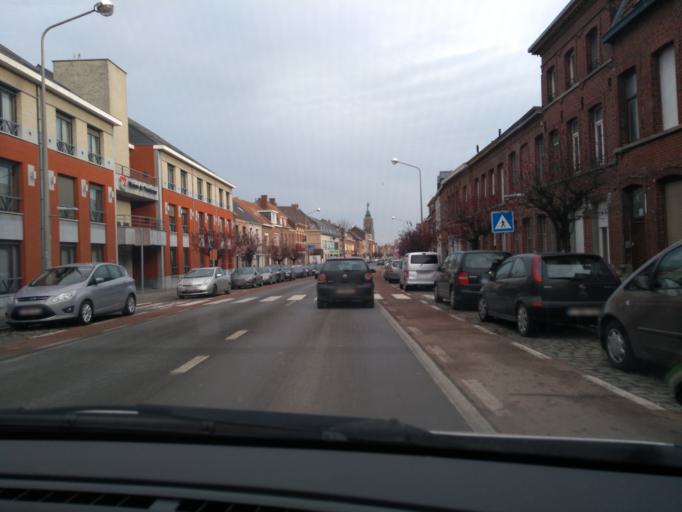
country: BE
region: Wallonia
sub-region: Province du Hainaut
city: Tournai
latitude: 50.6127
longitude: 3.4037
